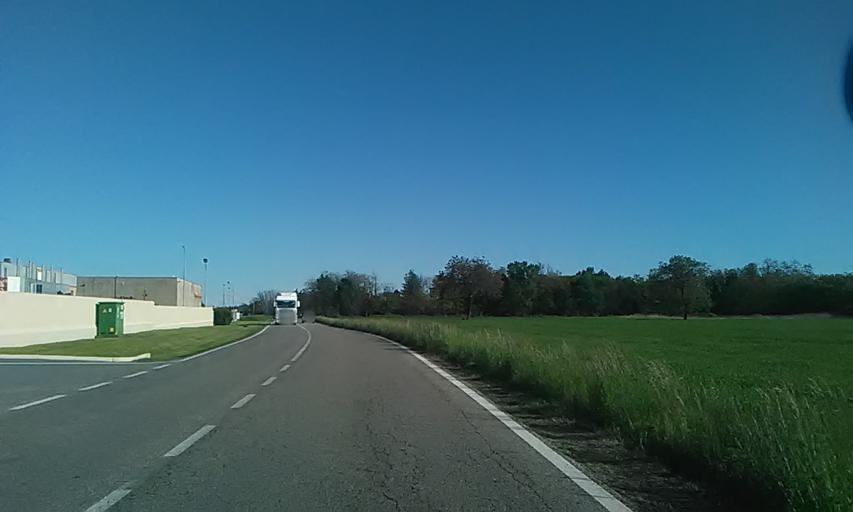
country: IT
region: Piedmont
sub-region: Provincia di Novara
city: Cavaglietto
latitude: 45.6062
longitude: 8.5250
